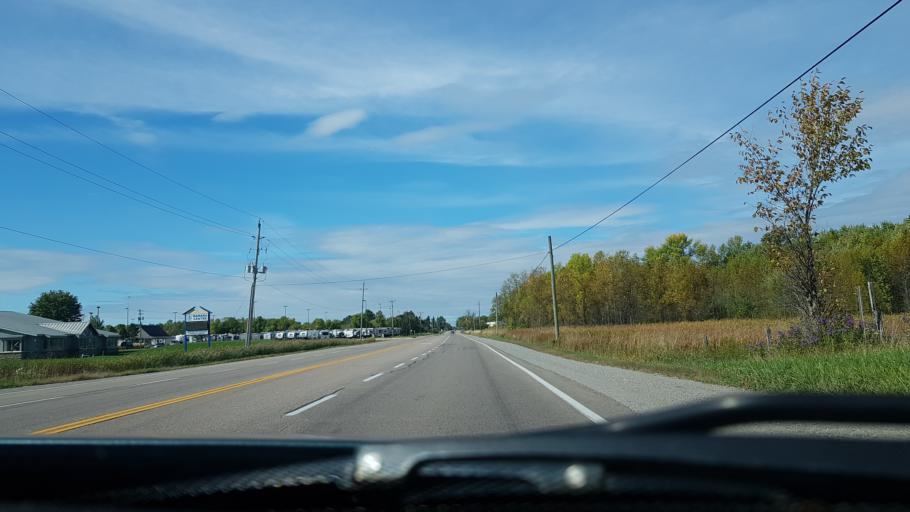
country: CA
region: Ontario
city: Orillia
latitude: 44.5996
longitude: -79.3341
